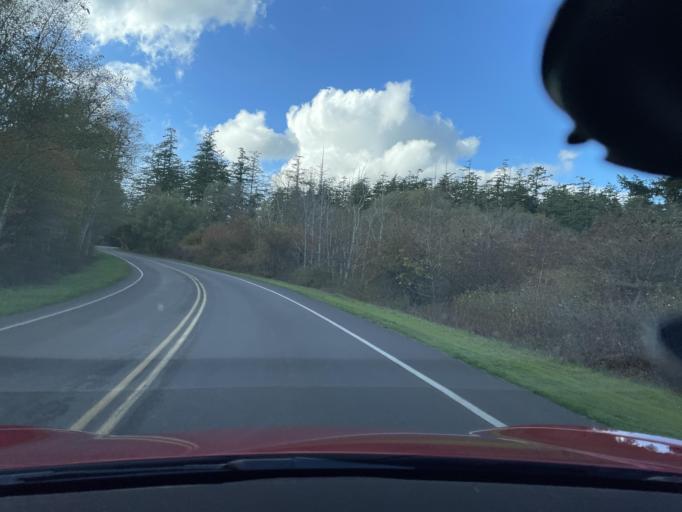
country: US
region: Washington
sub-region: San Juan County
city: Friday Harbor
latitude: 48.4686
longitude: -123.0084
